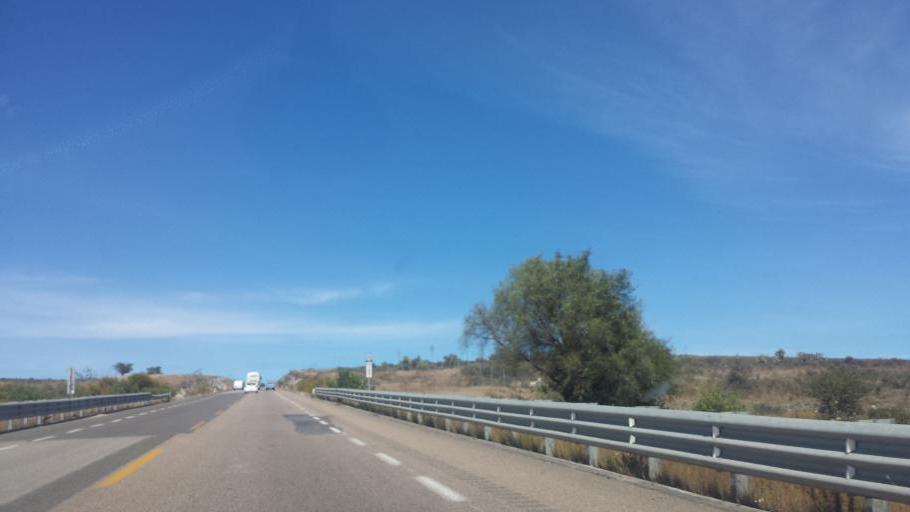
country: MX
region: Oaxaca
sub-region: Villa Tejupam de la Union
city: Villa Tejupam de la Union
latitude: 17.7683
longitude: -97.3572
